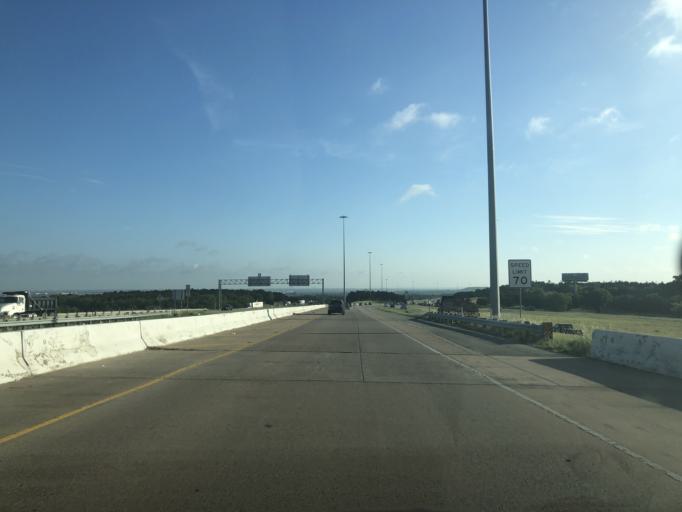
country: US
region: Texas
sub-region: Dallas County
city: Duncanville
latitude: 32.6733
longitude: -96.9468
